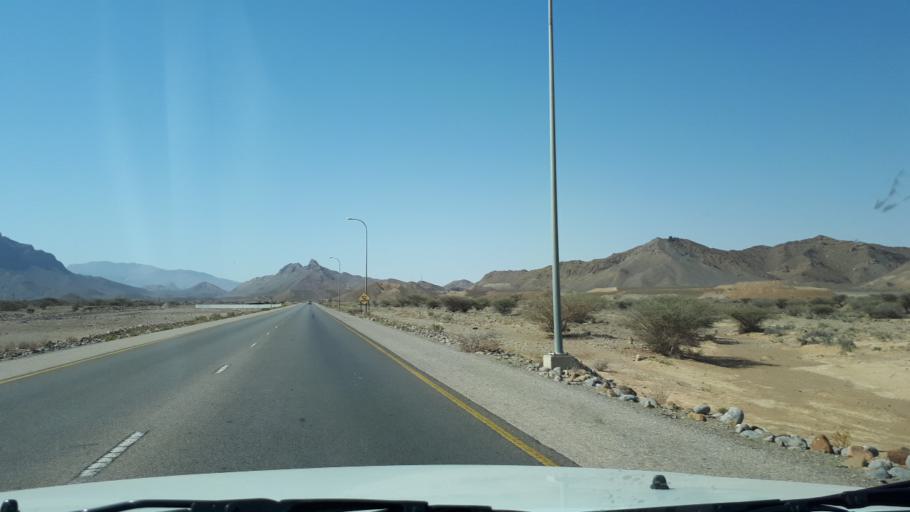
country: OM
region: Ash Sharqiyah
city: Sur
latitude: 22.3601
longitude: 59.3123
